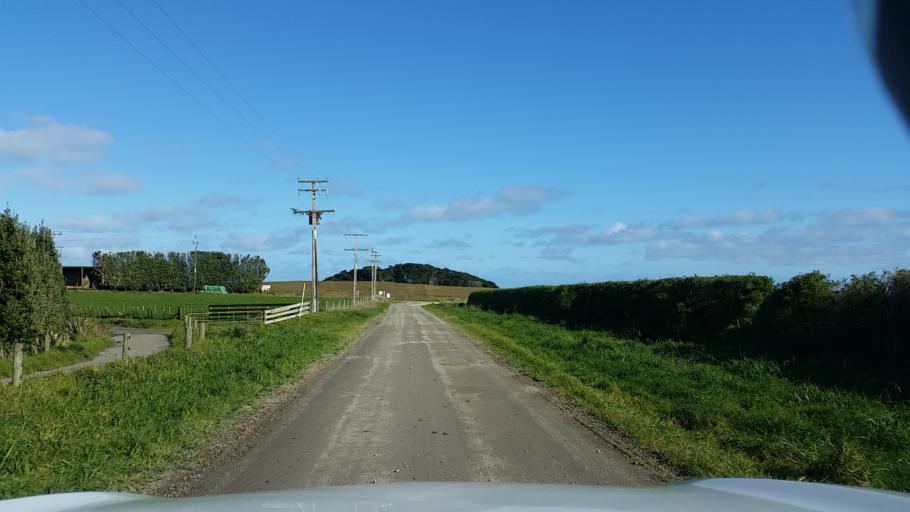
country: NZ
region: Taranaki
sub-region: South Taranaki District
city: Patea
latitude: -39.6860
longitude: 174.3977
